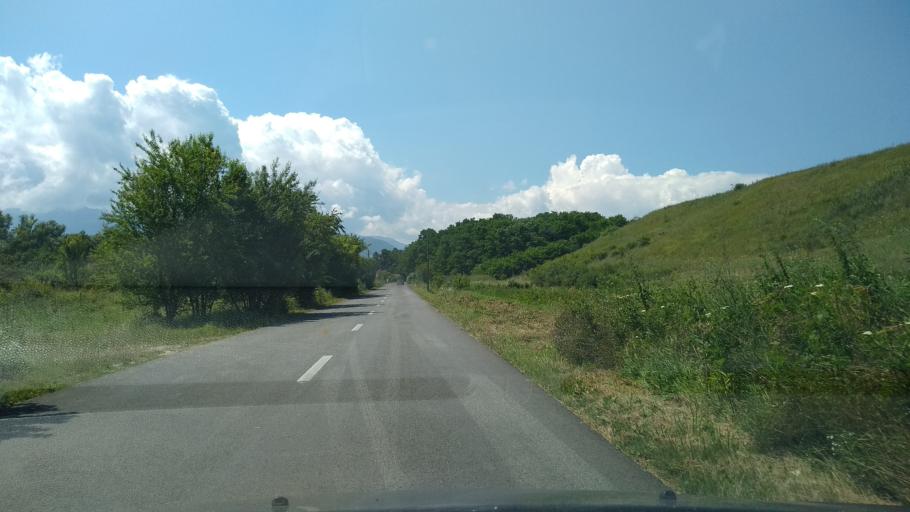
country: RO
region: Hunedoara
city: Salasu de Sus
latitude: 45.5376
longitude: 22.9780
